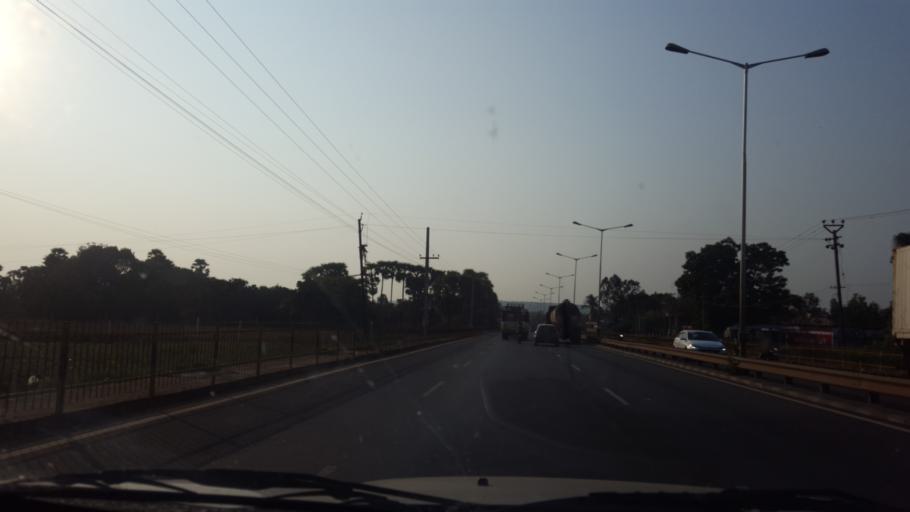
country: IN
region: Andhra Pradesh
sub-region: East Godavari
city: Pithapuram
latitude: 17.2424
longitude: 82.3591
